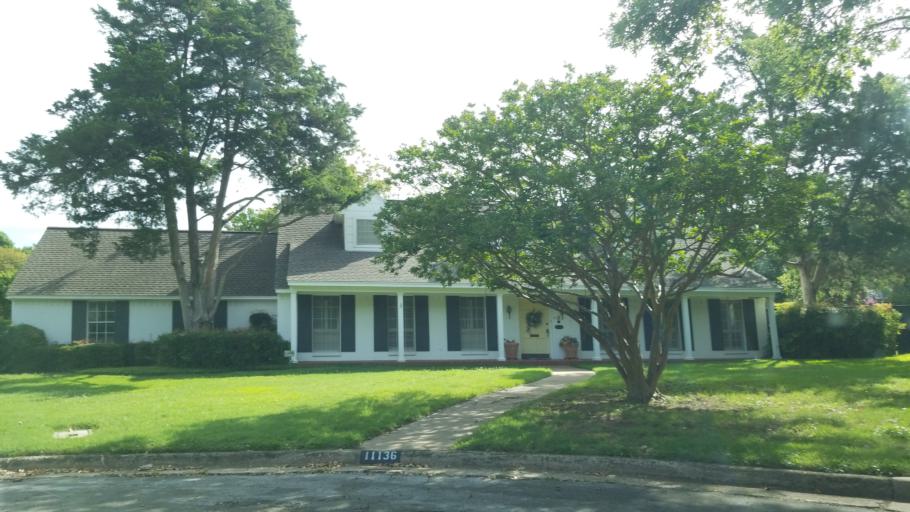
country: US
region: Texas
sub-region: Dallas County
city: Farmers Branch
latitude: 32.9003
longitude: -96.8471
